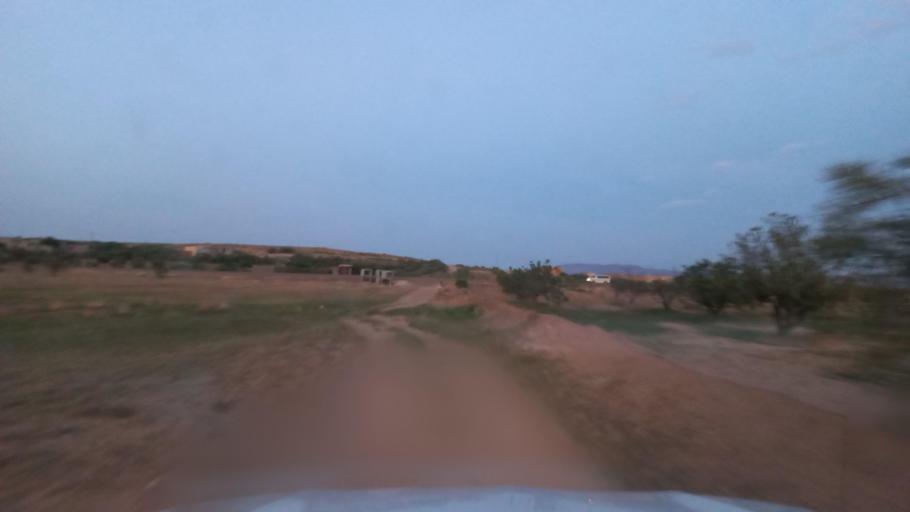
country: TN
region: Al Qasrayn
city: Sbiba
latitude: 35.3603
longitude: 9.0432
